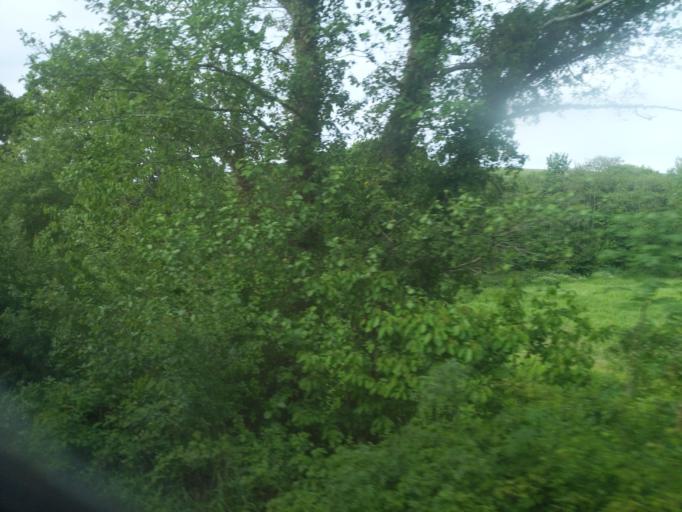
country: GB
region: England
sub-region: Devon
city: Barnstaple
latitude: 51.0412
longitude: -4.0424
